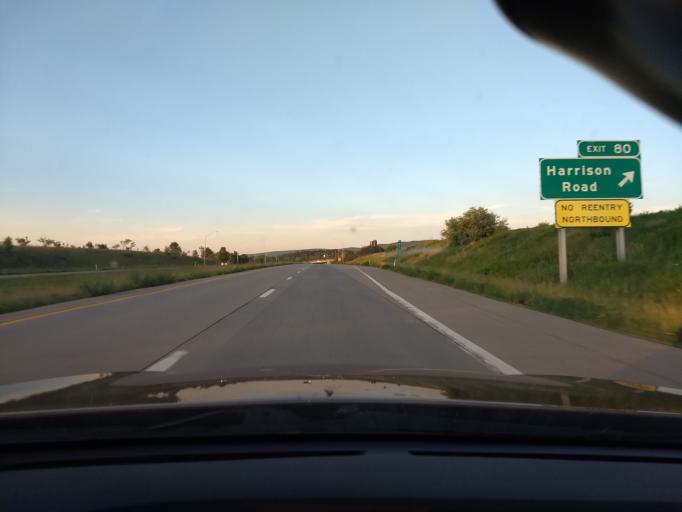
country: US
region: Pennsylvania
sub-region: Centre County
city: Pleasant Gap
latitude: 40.8823
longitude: -77.7492
